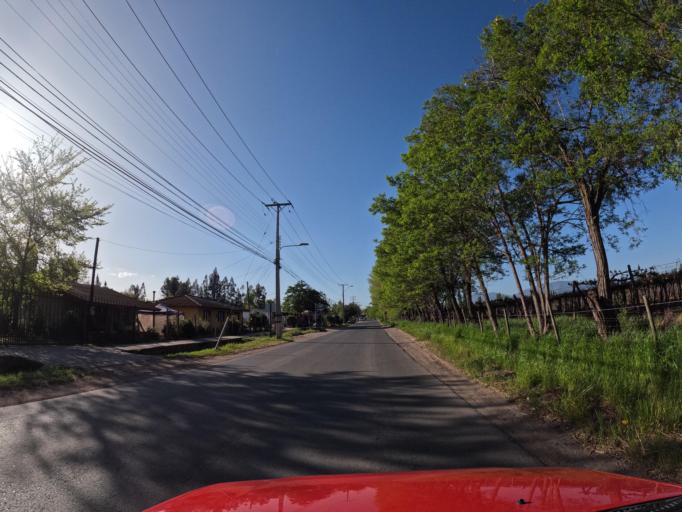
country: CL
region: O'Higgins
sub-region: Provincia de Colchagua
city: Santa Cruz
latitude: -34.7177
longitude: -71.2878
